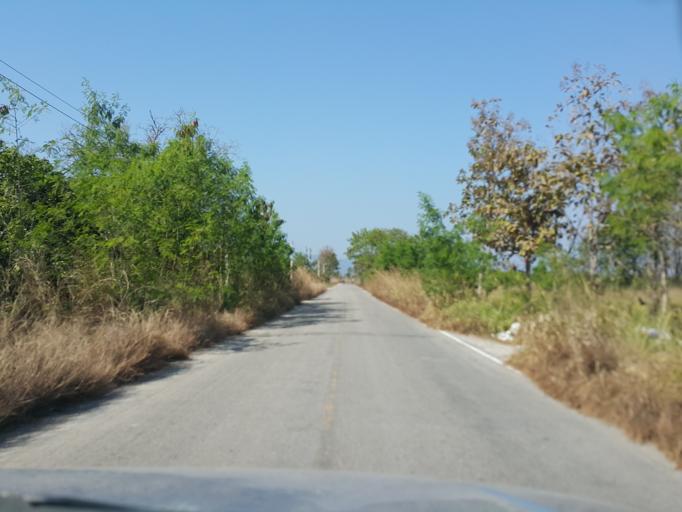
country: TH
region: Chiang Mai
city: Mae Wang
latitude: 18.5657
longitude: 98.7921
